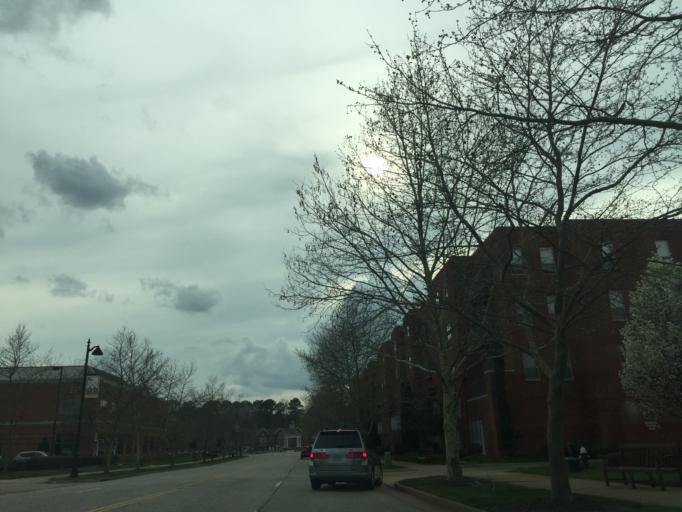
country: US
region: Virginia
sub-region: City of Newport News
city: Newport News
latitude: 37.0848
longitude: -76.4853
